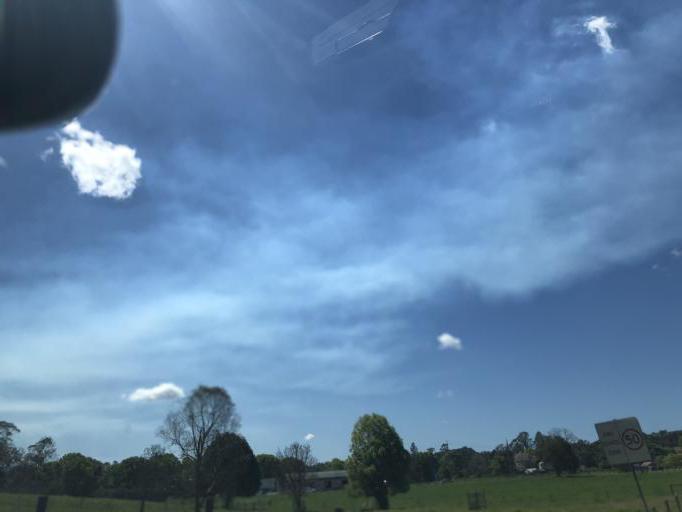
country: AU
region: New South Wales
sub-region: Bellingen
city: Bellingen
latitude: -30.4558
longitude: 152.9093
